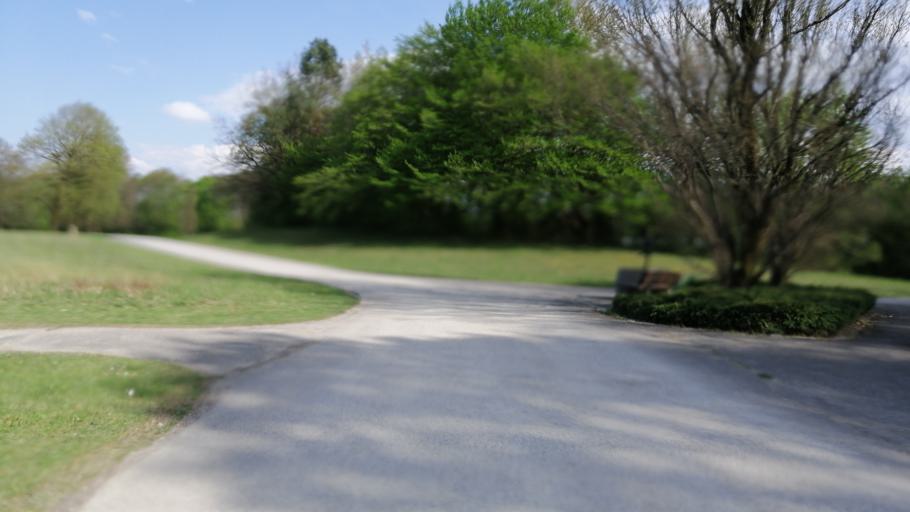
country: DE
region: Bavaria
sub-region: Upper Bavaria
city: Unterhaching
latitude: 48.0973
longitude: 11.6201
